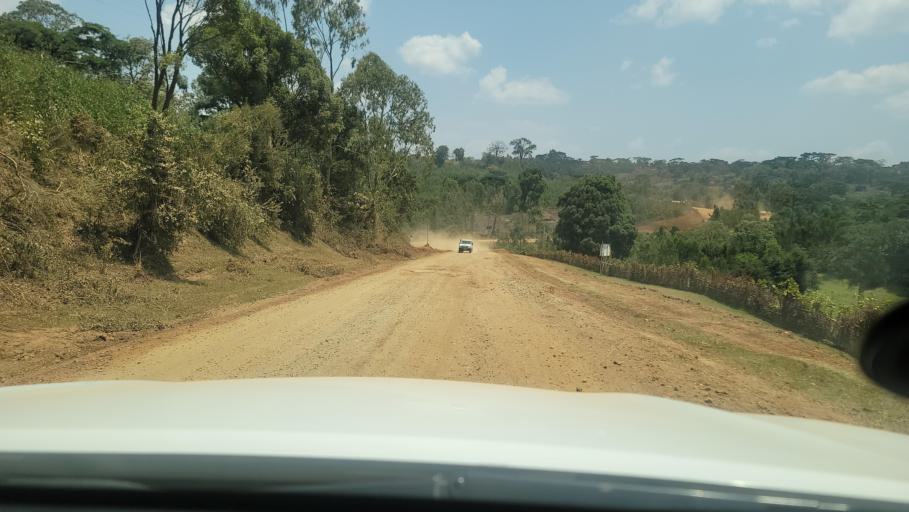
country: ET
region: Oromiya
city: Agaro
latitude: 7.7939
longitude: 36.4544
